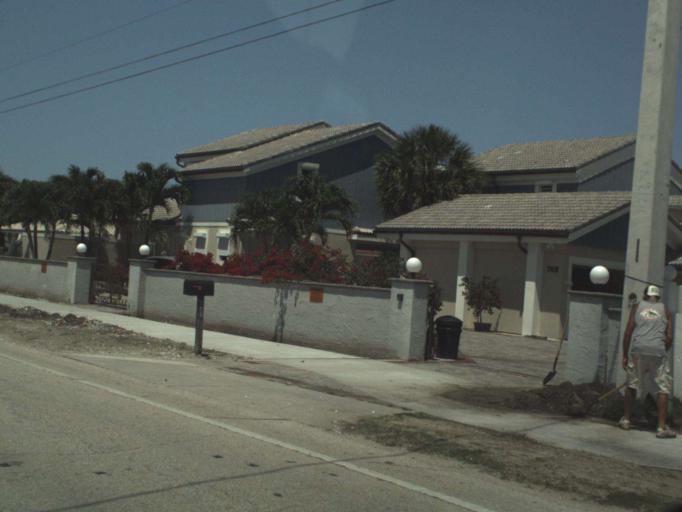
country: US
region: Florida
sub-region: Brevard County
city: Cocoa Beach
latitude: 28.3043
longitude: -80.6086
